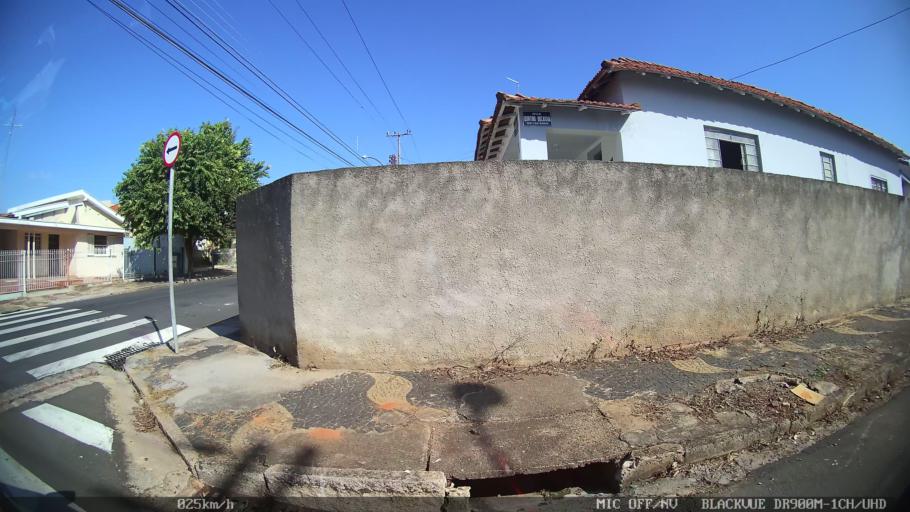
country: BR
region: Sao Paulo
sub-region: Americana
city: Americana
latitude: -22.7507
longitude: -47.3259
